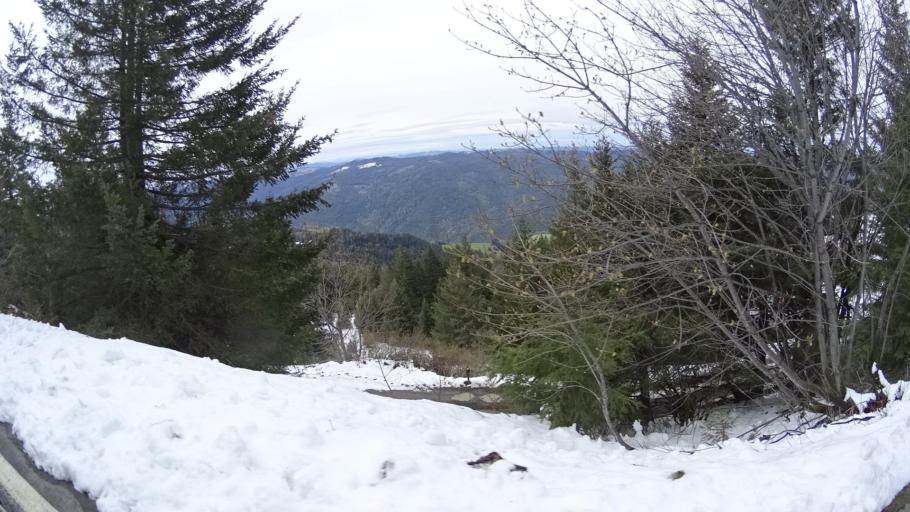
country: US
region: California
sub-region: Humboldt County
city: Willow Creek
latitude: 40.8687
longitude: -123.7480
